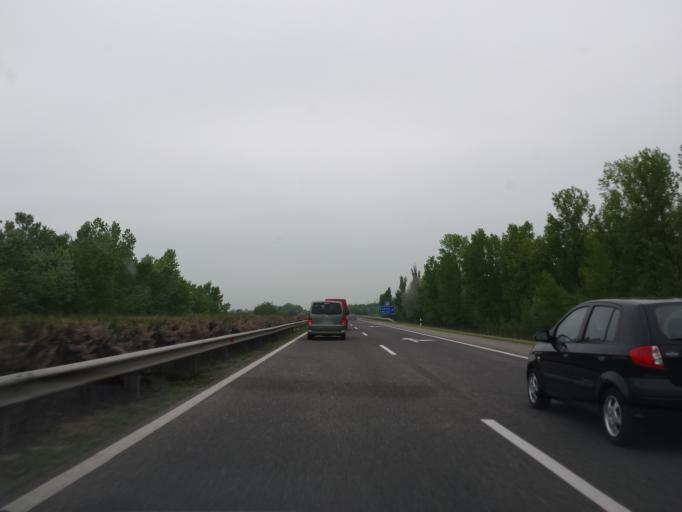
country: HU
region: Gyor-Moson-Sopron
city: Mosonszentmiklos
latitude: 47.7467
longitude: 17.4233
